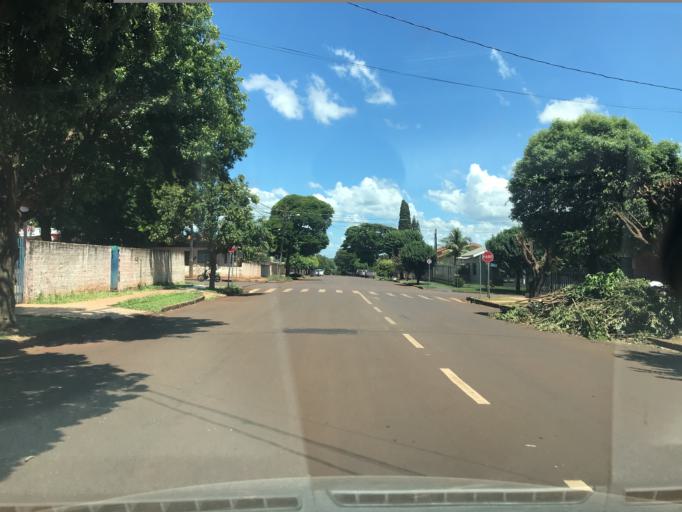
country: BR
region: Parana
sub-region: Palotina
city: Palotina
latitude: -24.2861
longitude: -53.8462
